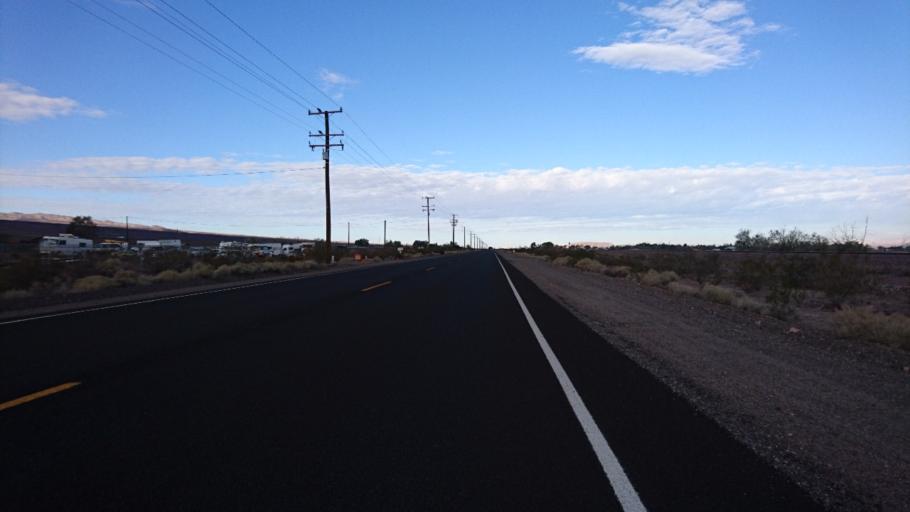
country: US
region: California
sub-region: San Bernardino County
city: Barstow
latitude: 34.8416
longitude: -116.7491
